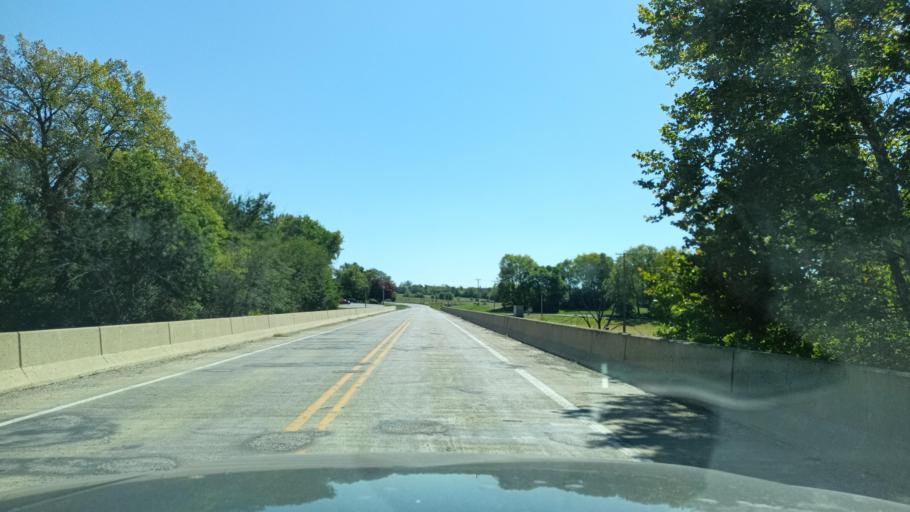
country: US
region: Illinois
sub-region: Woodford County
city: Eureka
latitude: 40.6238
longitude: -89.2419
